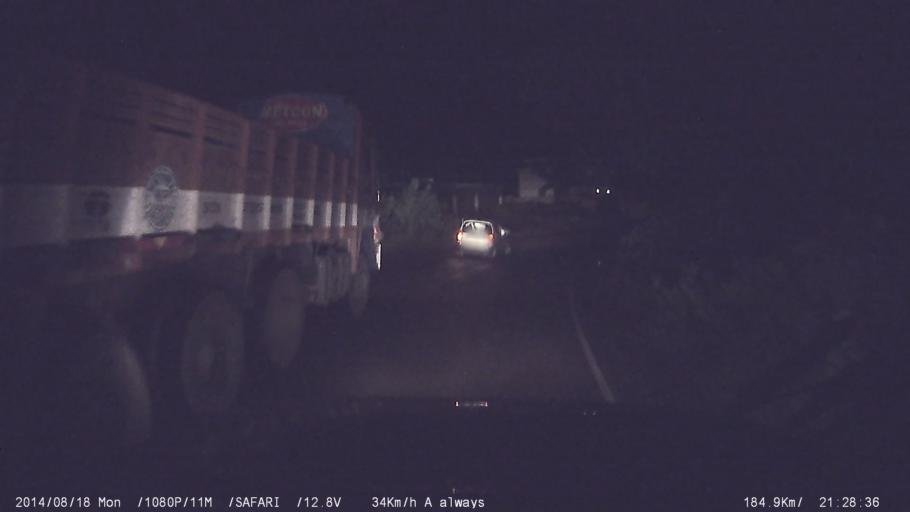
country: IN
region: Kerala
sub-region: Thrissur District
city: Chelakara
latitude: 10.5740
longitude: 76.3881
